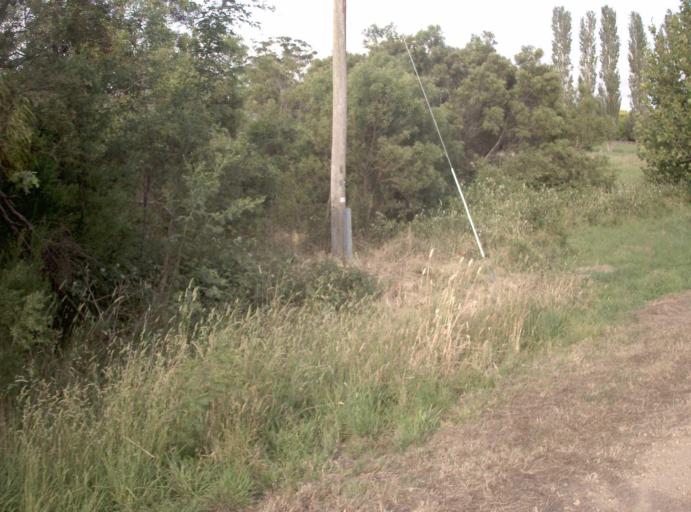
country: AU
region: Victoria
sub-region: Wellington
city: Heyfield
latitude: -37.9654
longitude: 146.9037
